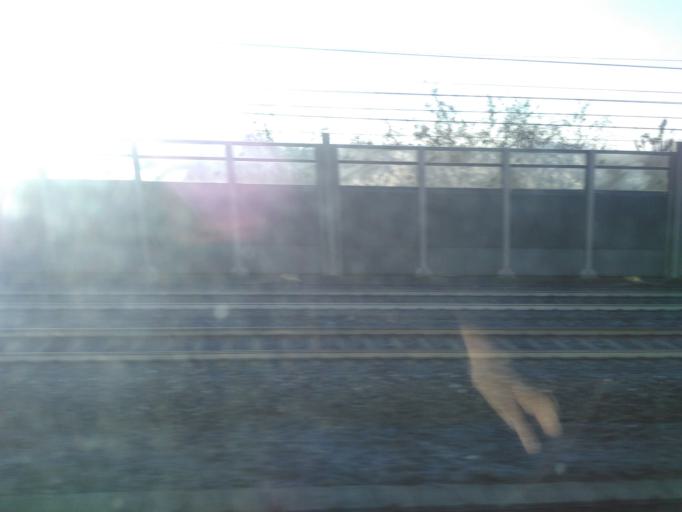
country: IT
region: Veneto
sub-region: Provincia di Padova
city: Vigonza
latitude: 45.4378
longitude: 11.9923
